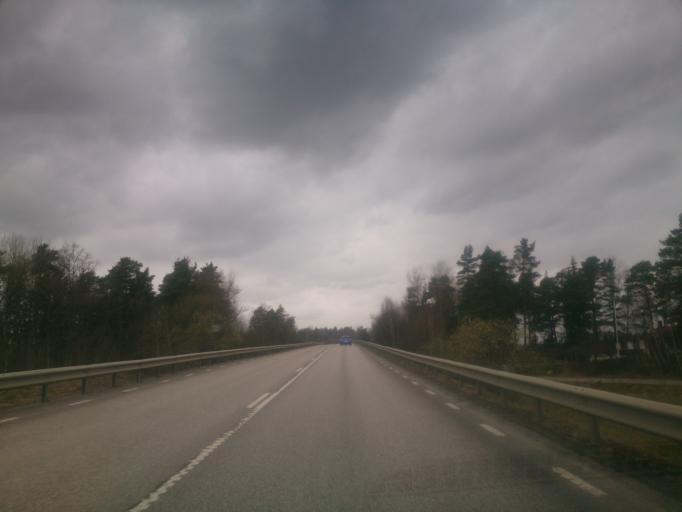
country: SE
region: OEstergoetland
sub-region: Norrkopings Kommun
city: Svartinge
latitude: 58.5786
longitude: 16.0421
